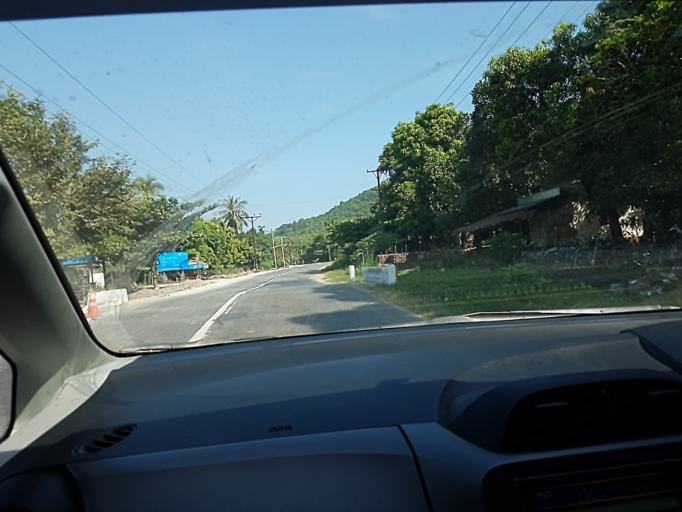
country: MM
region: Mon
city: Thaton
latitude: 16.7386
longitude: 97.4108
